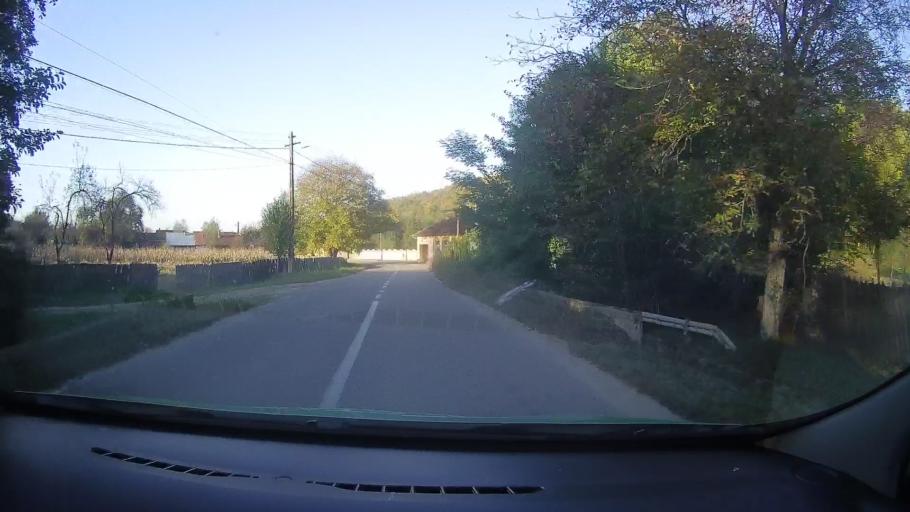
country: RO
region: Timis
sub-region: Comuna Fardea
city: Fardea
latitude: 45.7161
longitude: 22.1581
